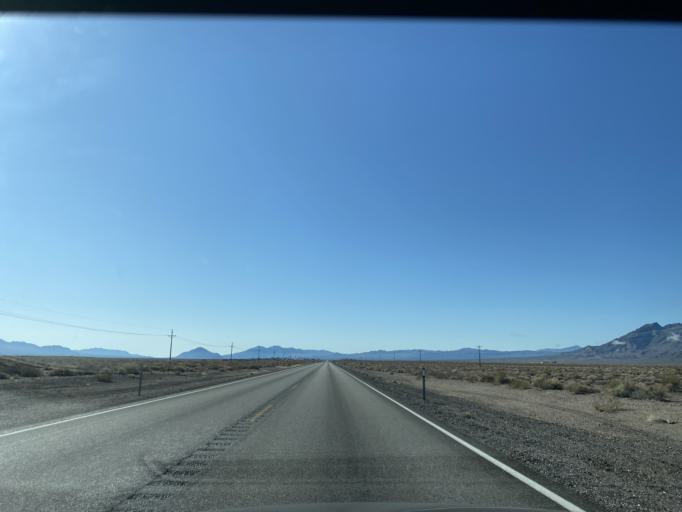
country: US
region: Nevada
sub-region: Nye County
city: Pahrump
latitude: 36.4428
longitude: -116.4220
